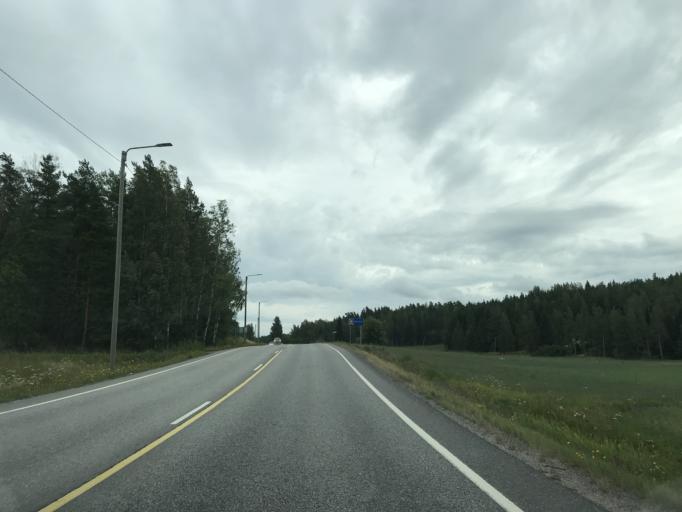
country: FI
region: Varsinais-Suomi
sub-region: Turku
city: Piikkioe
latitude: 60.4330
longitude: 22.5981
